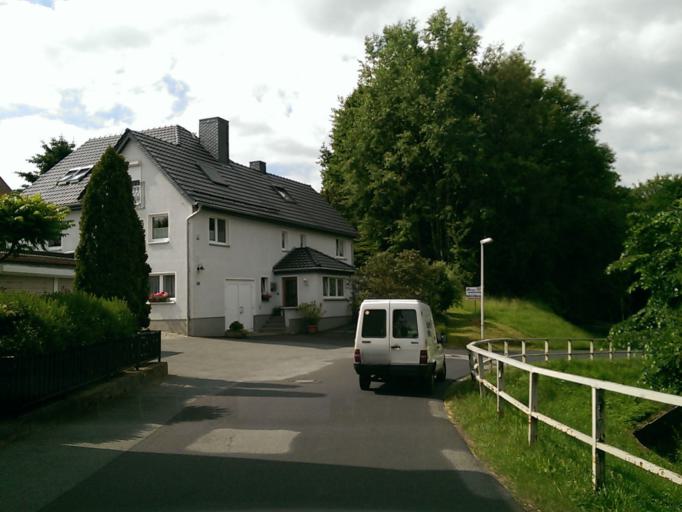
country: DE
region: Saxony
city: Mittelherwigsdorf
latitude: 50.9197
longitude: 14.7662
